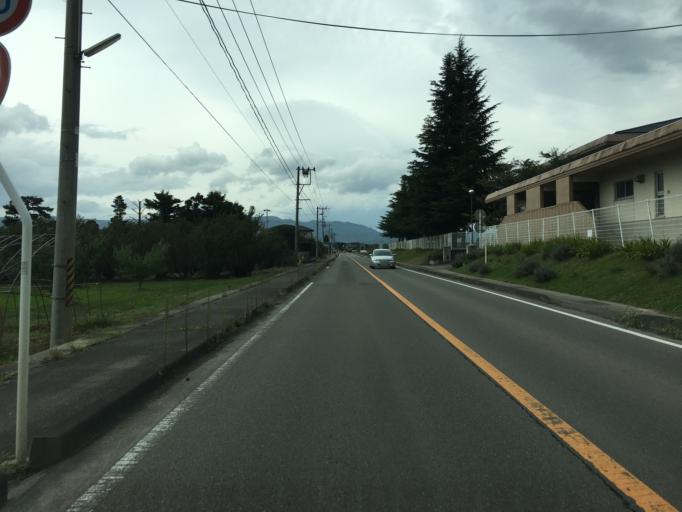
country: JP
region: Fukushima
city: Hobaramachi
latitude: 37.8324
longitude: 140.5579
